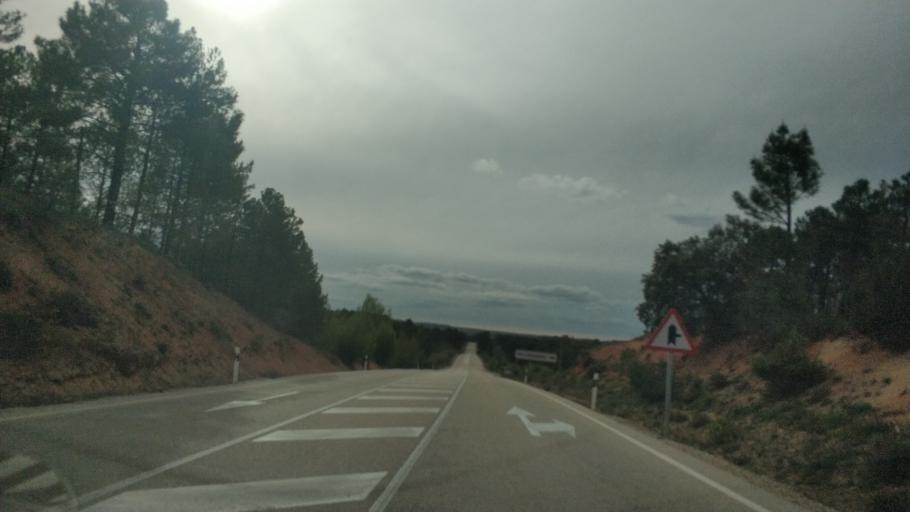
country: ES
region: Castille and Leon
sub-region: Provincia de Soria
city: Valdenebro
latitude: 41.5589
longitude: -2.9704
